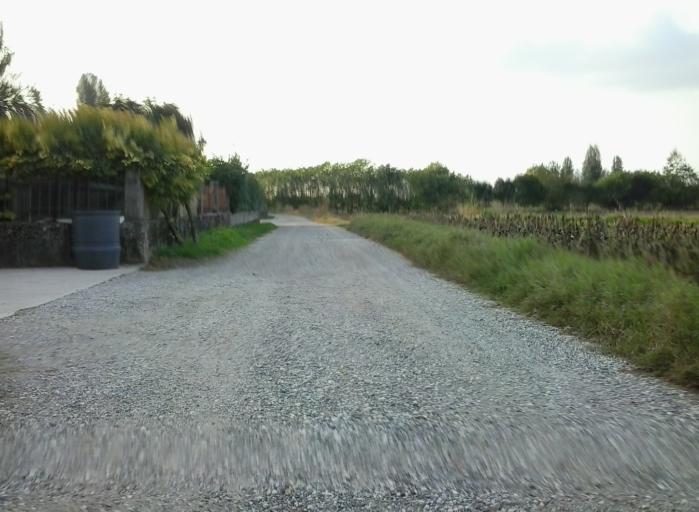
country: IT
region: Lombardy
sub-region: Provincia di Brescia
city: Azzano Mella
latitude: 45.4263
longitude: 10.1143
